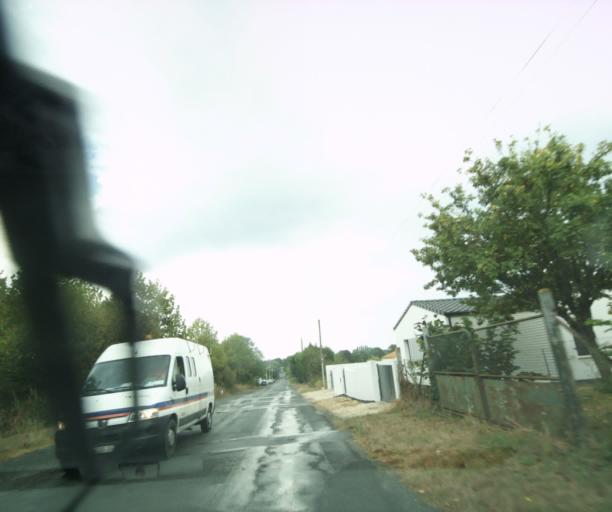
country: FR
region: Poitou-Charentes
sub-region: Departement de la Charente-Maritime
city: Tonnay-Charente
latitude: 45.9433
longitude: -0.8807
